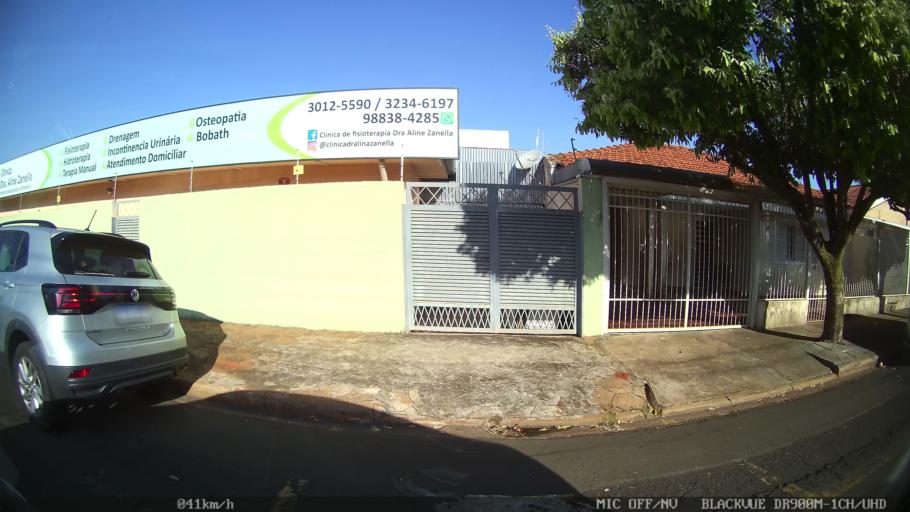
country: BR
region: Sao Paulo
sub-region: Sao Jose Do Rio Preto
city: Sao Jose do Rio Preto
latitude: -20.8117
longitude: -49.3971
